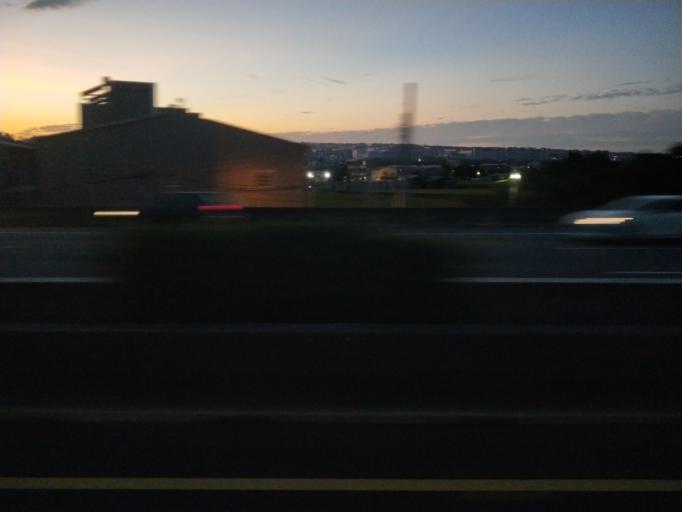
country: TW
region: Taiwan
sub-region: Taichung City
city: Taichung
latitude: 24.1904
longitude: 120.6385
